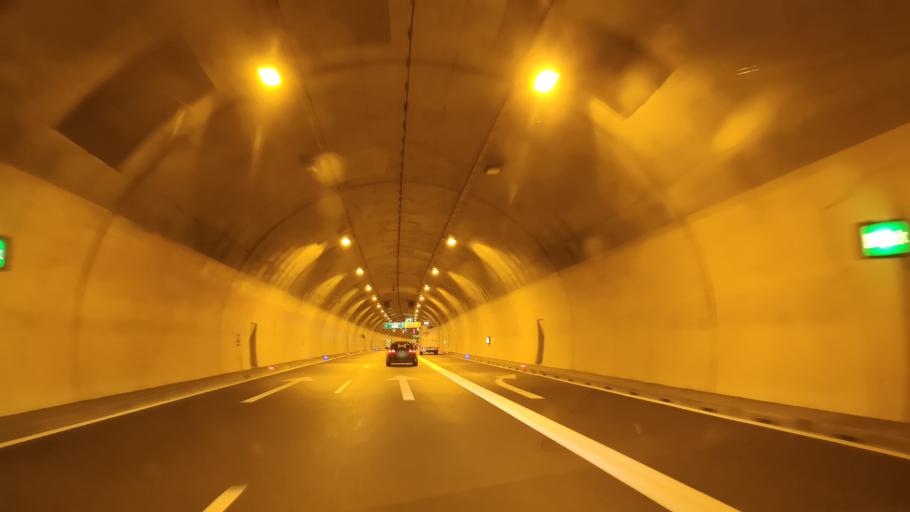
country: SI
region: Ljubljana
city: Ljubljana
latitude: 46.0903
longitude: 14.4608
